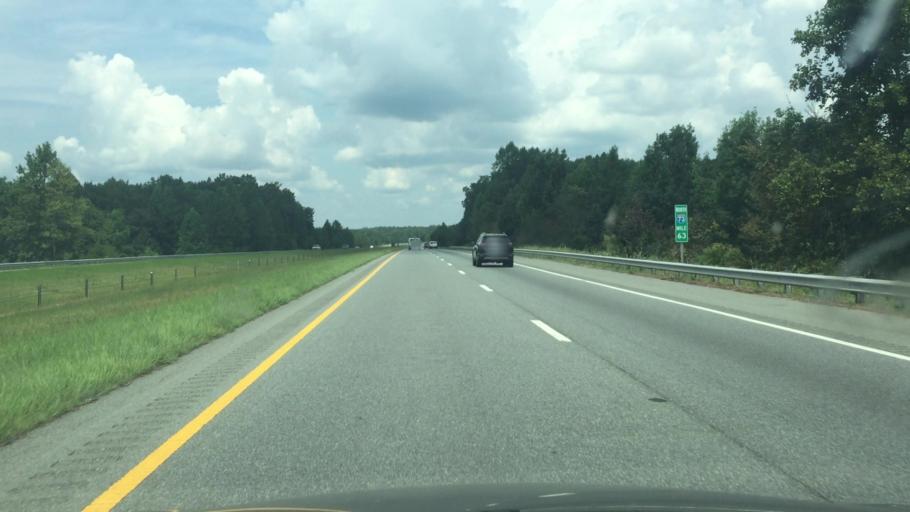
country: US
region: North Carolina
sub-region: Randolph County
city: Asheboro
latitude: 35.5532
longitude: -79.7993
